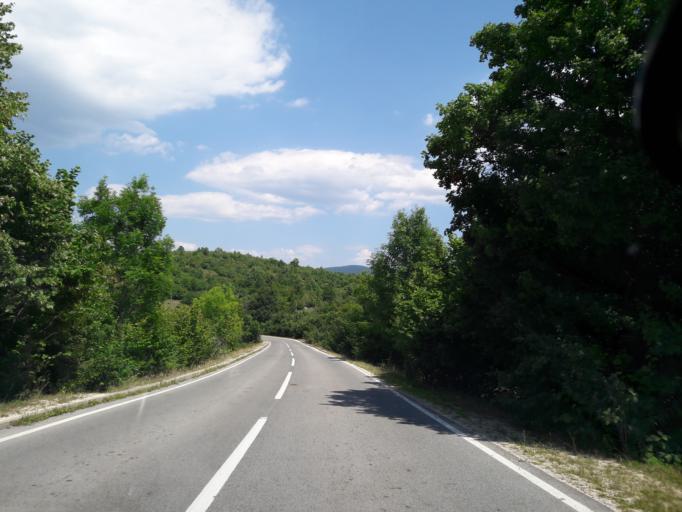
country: BA
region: Republika Srpska
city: Sipovo
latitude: 44.1379
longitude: 17.1789
